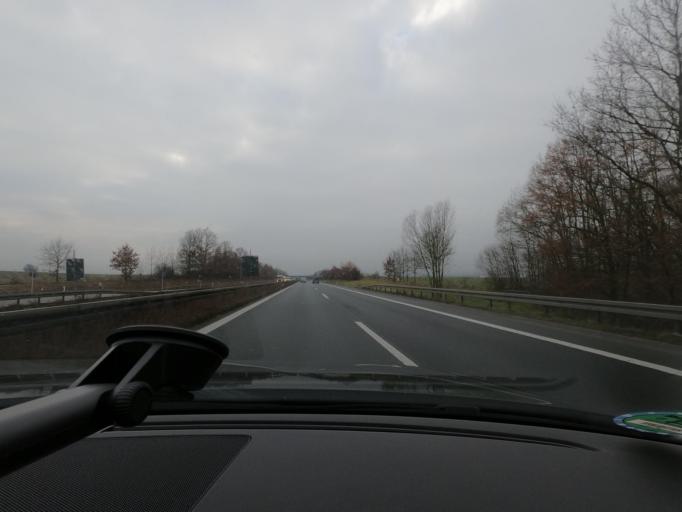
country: DE
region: Bavaria
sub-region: Upper Franconia
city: Hirschaid
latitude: 49.8219
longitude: 11.0096
